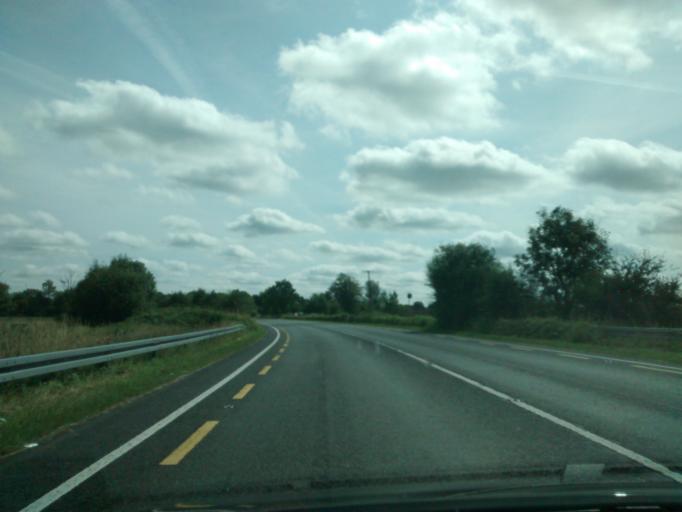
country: IE
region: Leinster
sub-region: Uibh Fhaili
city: Clara
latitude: 53.3673
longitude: -7.6392
